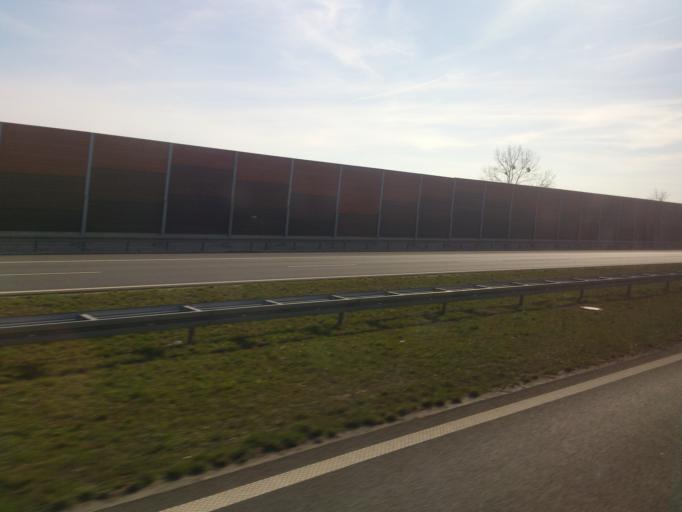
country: PL
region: Kujawsko-Pomorskie
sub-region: Powiat aleksandrowski
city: Waganiec
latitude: 52.8010
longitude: 18.8245
